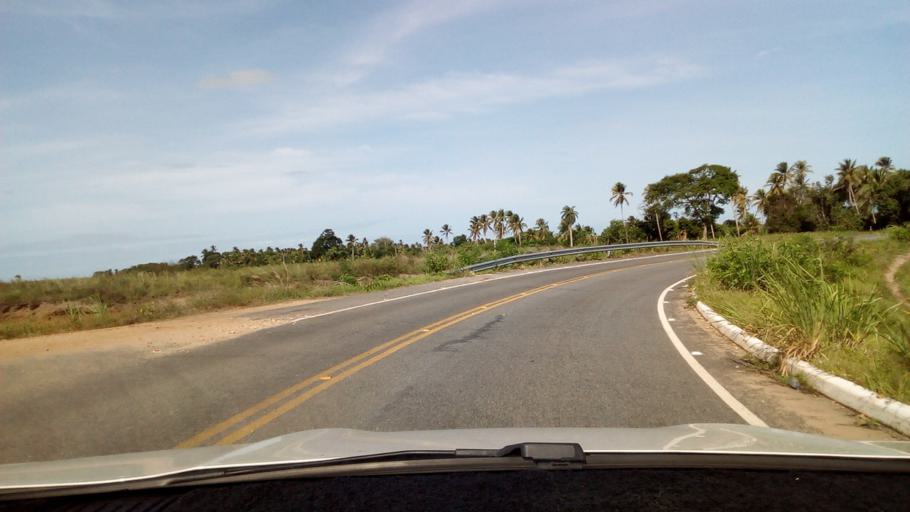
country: BR
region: Paraiba
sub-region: Bayeux
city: Bayeux
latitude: -7.0507
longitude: -34.9099
